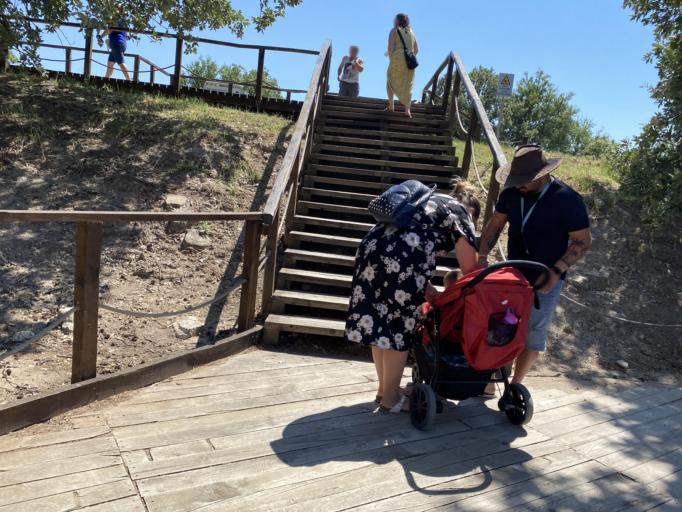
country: TR
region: Canakkale
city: Intepe
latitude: 39.9568
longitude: 26.2376
